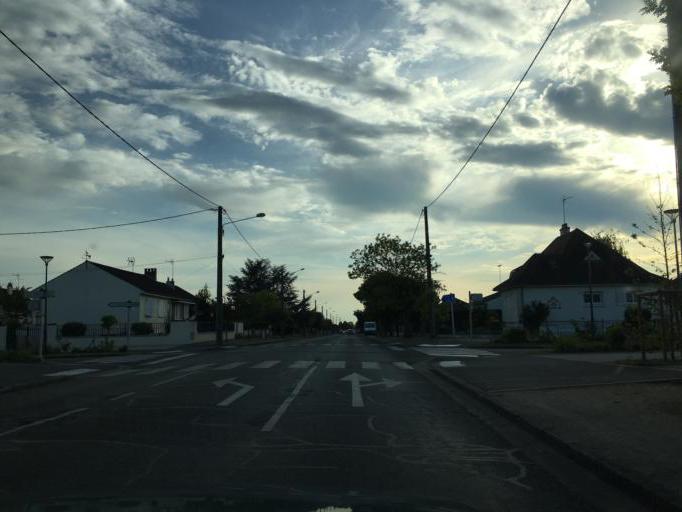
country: FR
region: Centre
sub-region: Departement du Loiret
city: Saint-Jean-de-la-Ruelle
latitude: 47.9147
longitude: 1.8629
